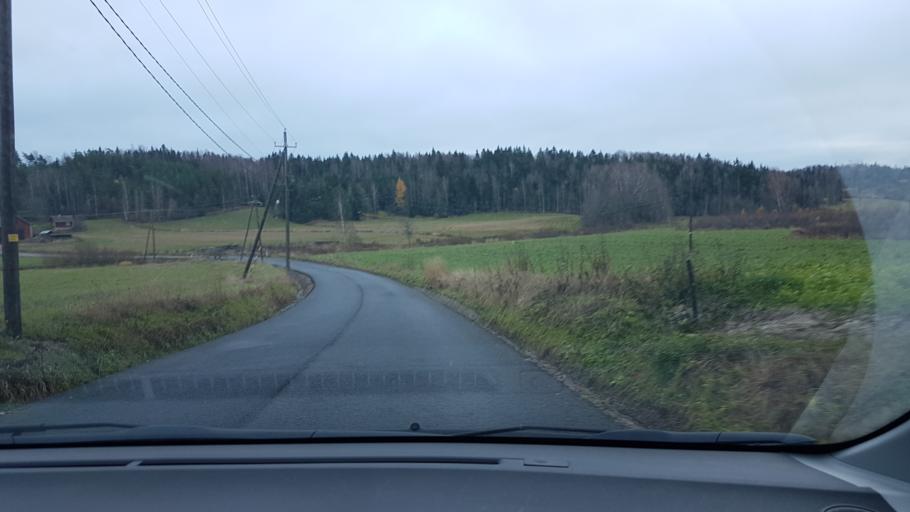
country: FI
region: Uusimaa
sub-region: Helsinki
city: Vantaa
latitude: 60.2827
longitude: 25.1422
